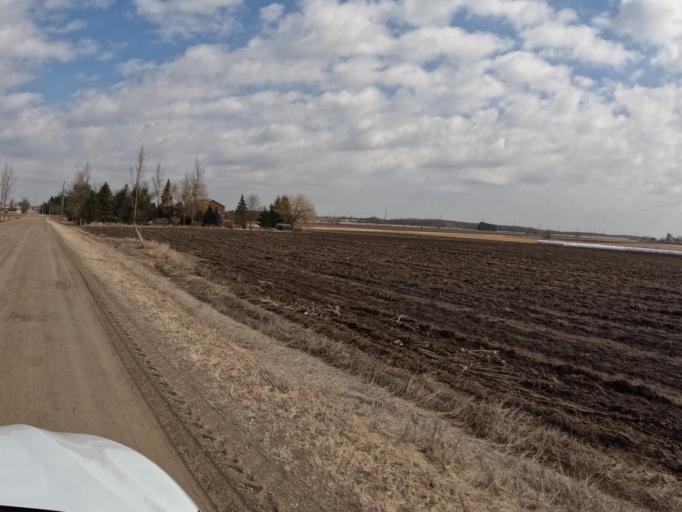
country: CA
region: Ontario
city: Orangeville
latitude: 43.9162
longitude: -80.2384
